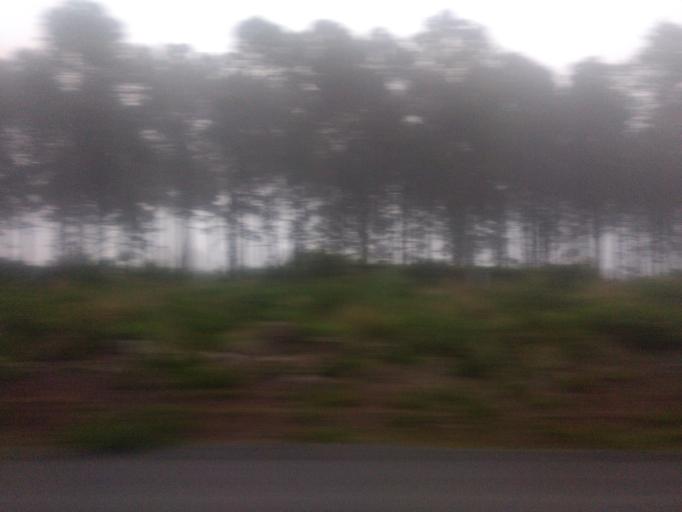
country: MX
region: Veracruz
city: Las Vigas
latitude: 19.6302
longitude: -97.1091
